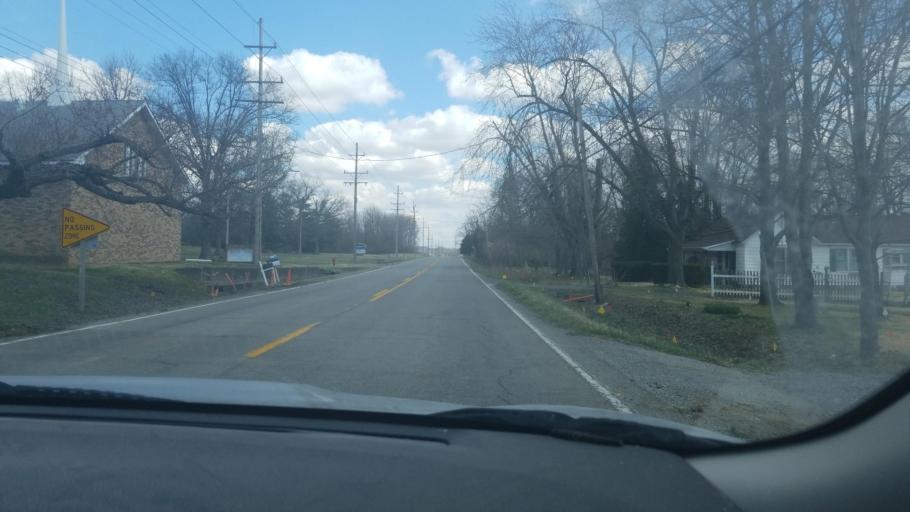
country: US
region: Illinois
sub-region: Saline County
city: Harrisburg
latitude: 37.7388
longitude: -88.5708
